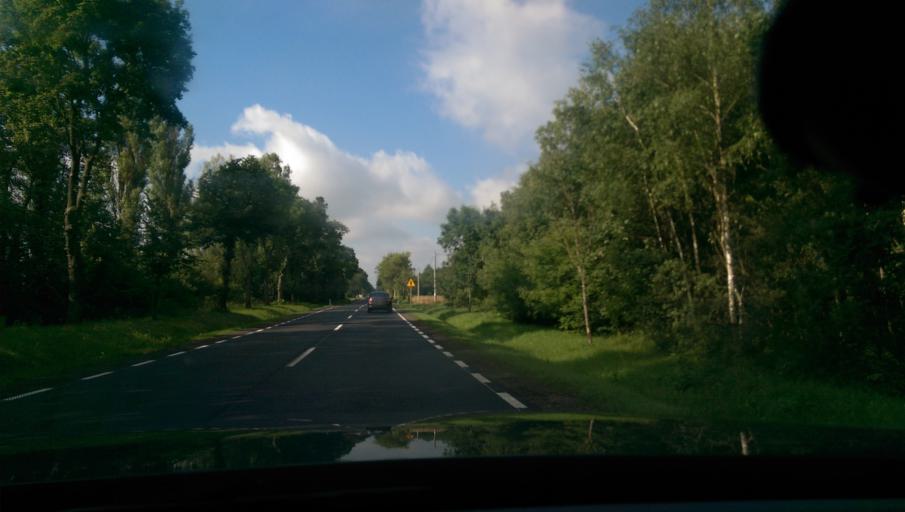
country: PL
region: Masovian Voivodeship
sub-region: Powiat ciechanowski
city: Ojrzen
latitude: 52.7498
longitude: 20.5314
